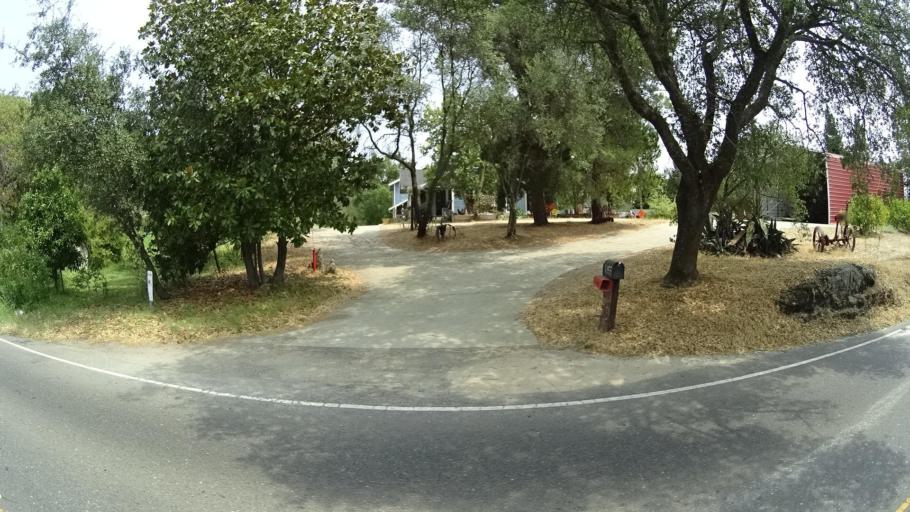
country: US
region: California
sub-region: Placer County
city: Granite Bay
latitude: 38.7746
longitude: -121.1918
